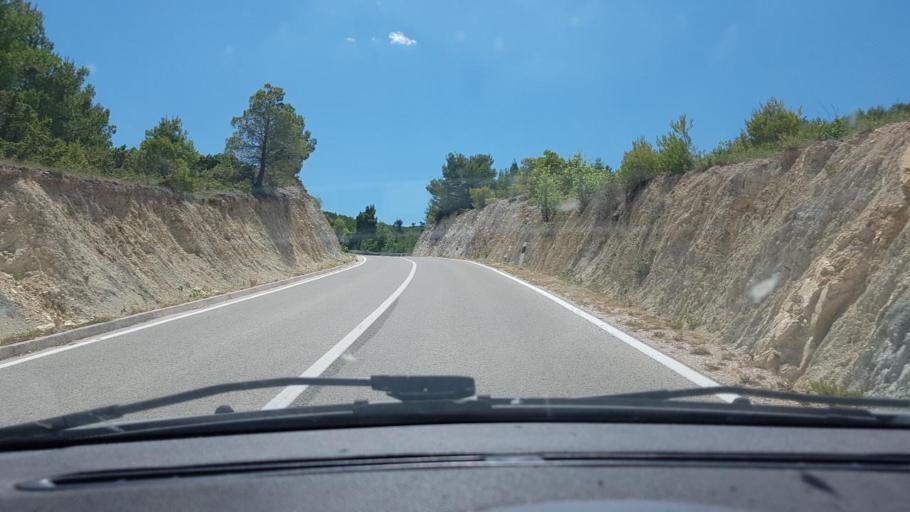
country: HR
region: Sibensko-Kniniska
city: Kistanje
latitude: 43.9061
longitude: 15.9135
